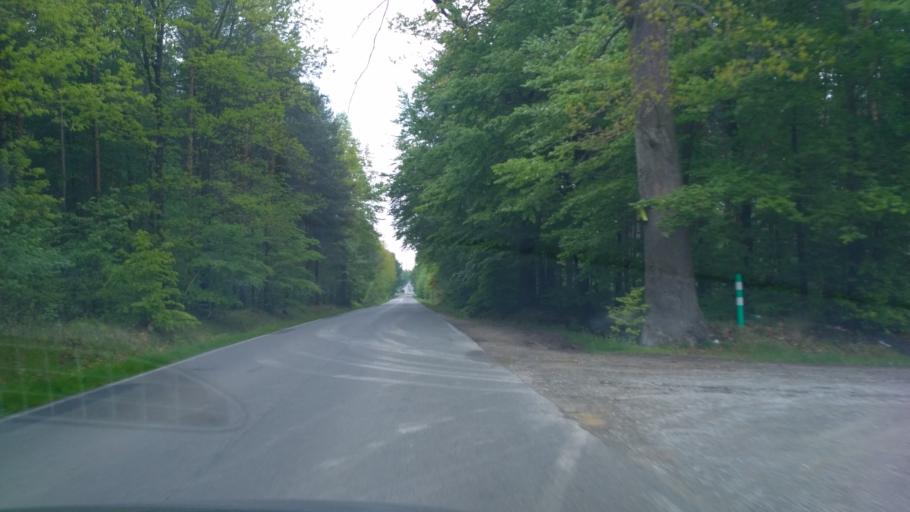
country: PL
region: Subcarpathian Voivodeship
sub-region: Powiat kolbuszowski
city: Kolbuszowa
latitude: 50.1733
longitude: 21.7594
